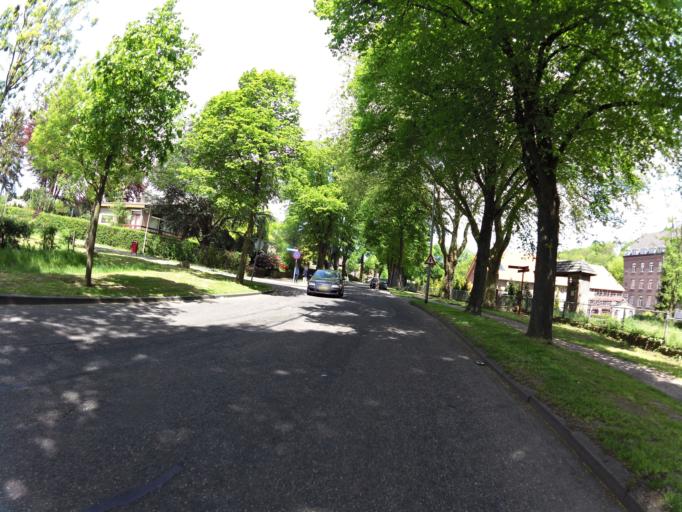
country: NL
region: Limburg
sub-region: Gemeente Kerkrade
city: Kerkrade
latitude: 50.8653
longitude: 6.0544
